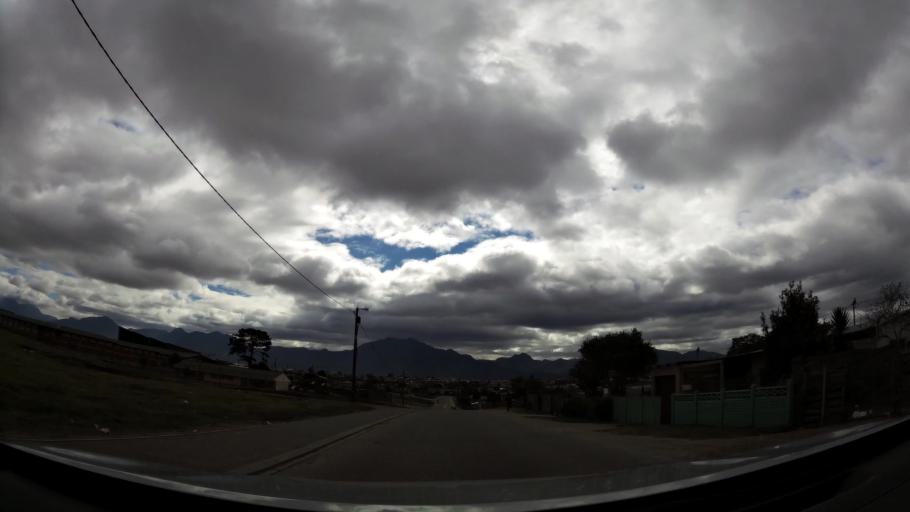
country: ZA
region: Western Cape
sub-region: Eden District Municipality
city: George
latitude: -34.0172
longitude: 22.4777
